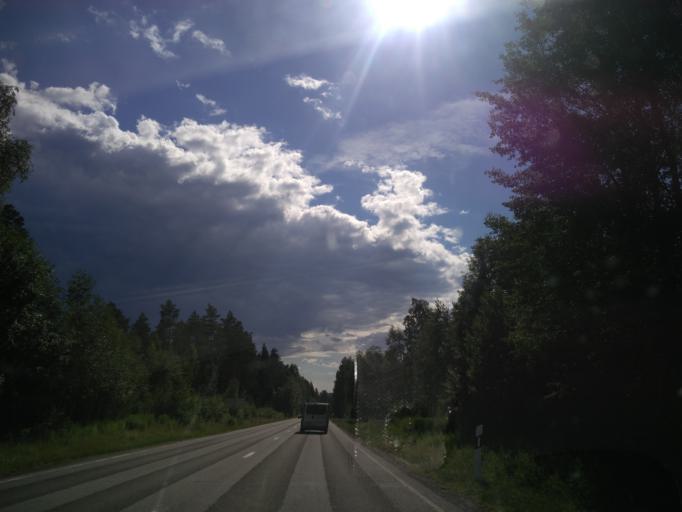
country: SE
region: OErebro
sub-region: Hallefors Kommun
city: Haellefors
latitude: 59.7466
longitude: 14.4972
